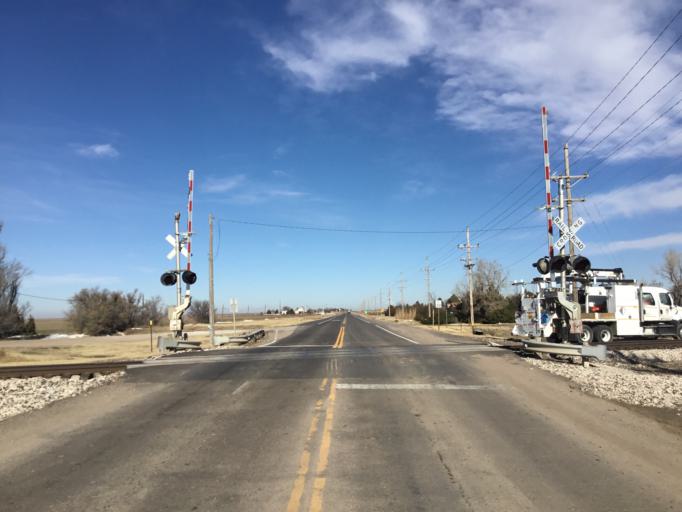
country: US
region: Kansas
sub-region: Ford County
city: Dodge City
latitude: 37.4445
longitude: -100.0153
